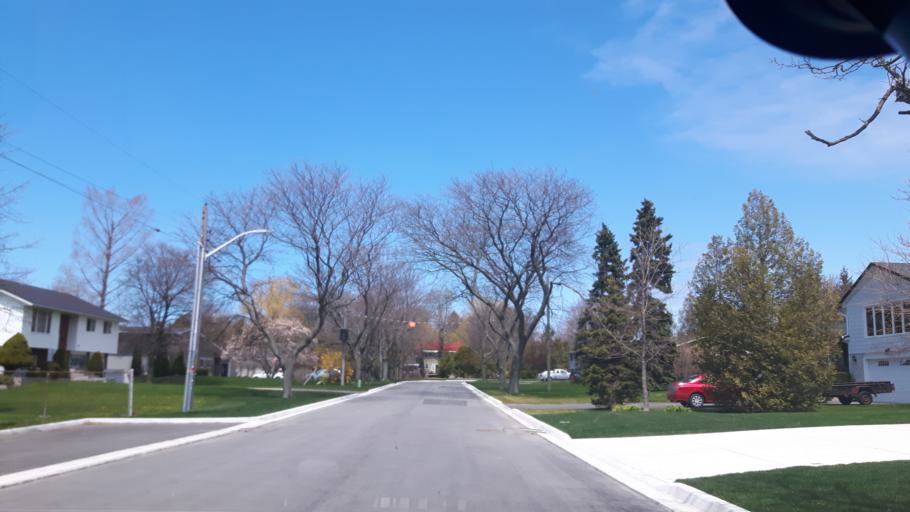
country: CA
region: Ontario
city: Goderich
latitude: 43.7318
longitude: -81.7227
